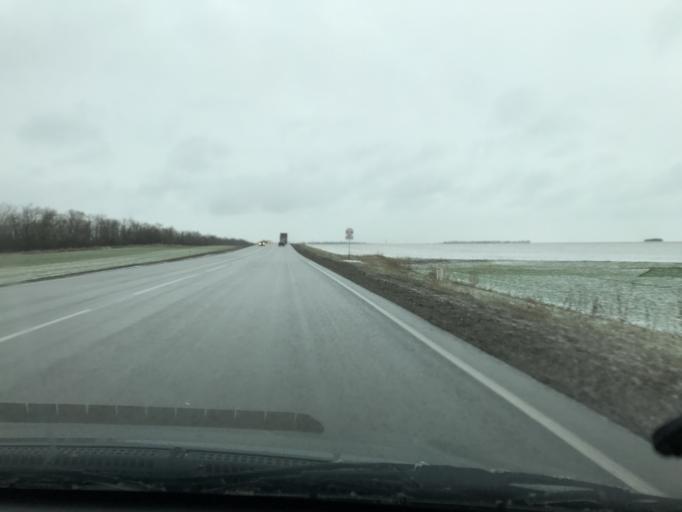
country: RU
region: Rostov
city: Kagal'nitskaya
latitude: 46.9046
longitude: 40.1194
